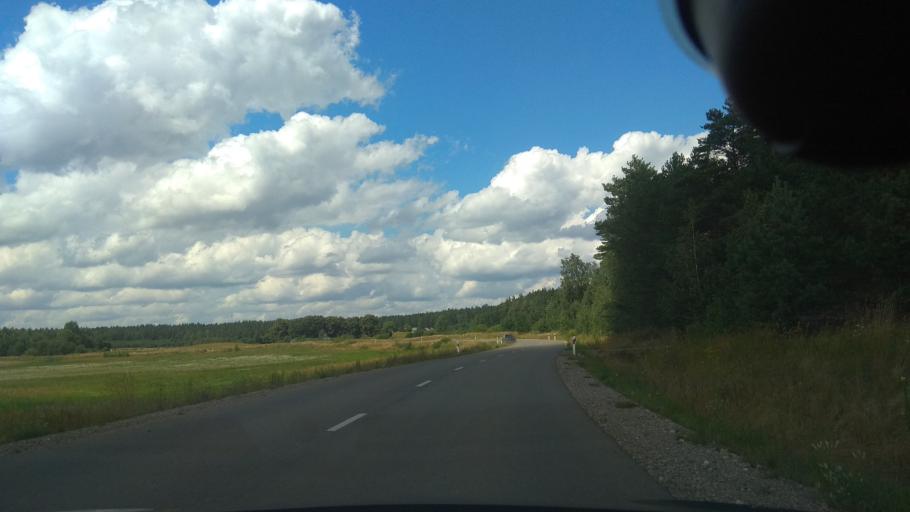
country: LT
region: Vilnius County
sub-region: Trakai
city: Rudiskes
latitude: 54.5096
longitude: 24.8643
